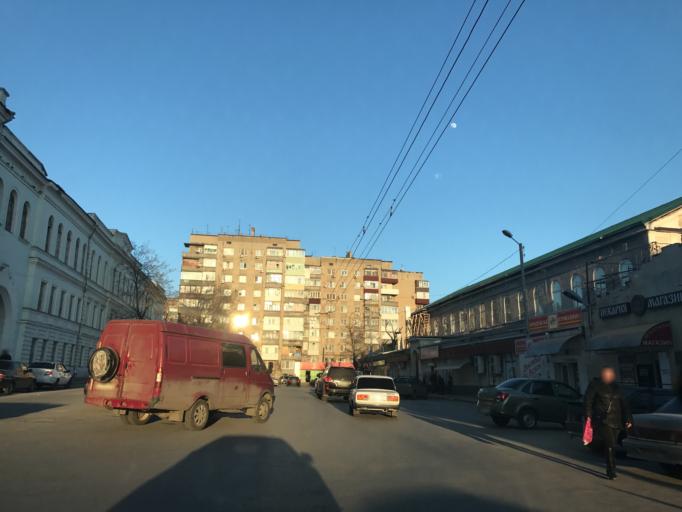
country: RU
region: Rostov
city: Rostov-na-Donu
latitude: 47.2332
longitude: 39.7636
